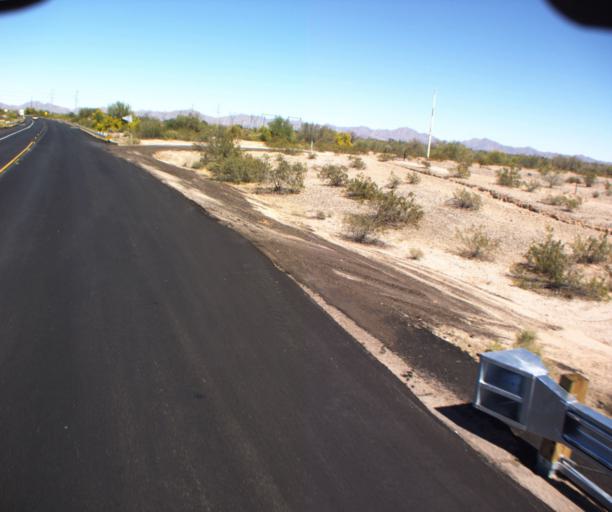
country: US
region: Arizona
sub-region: Maricopa County
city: Gila Bend
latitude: 32.9649
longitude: -112.6761
